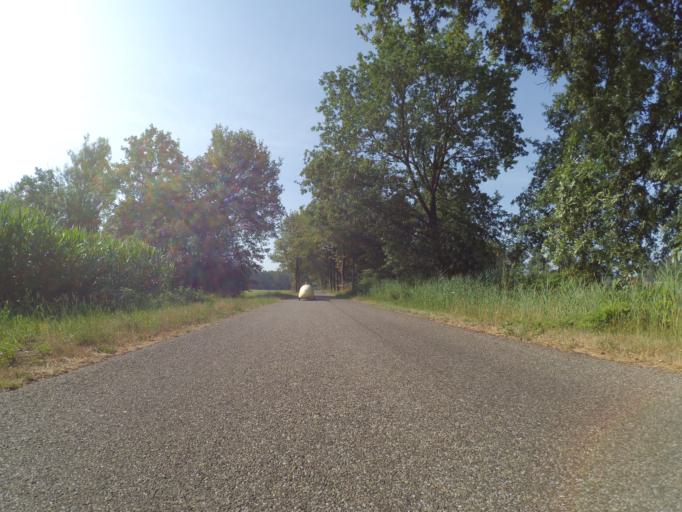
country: DE
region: Lower Saxony
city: Getelo
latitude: 52.3895
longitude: 6.8873
